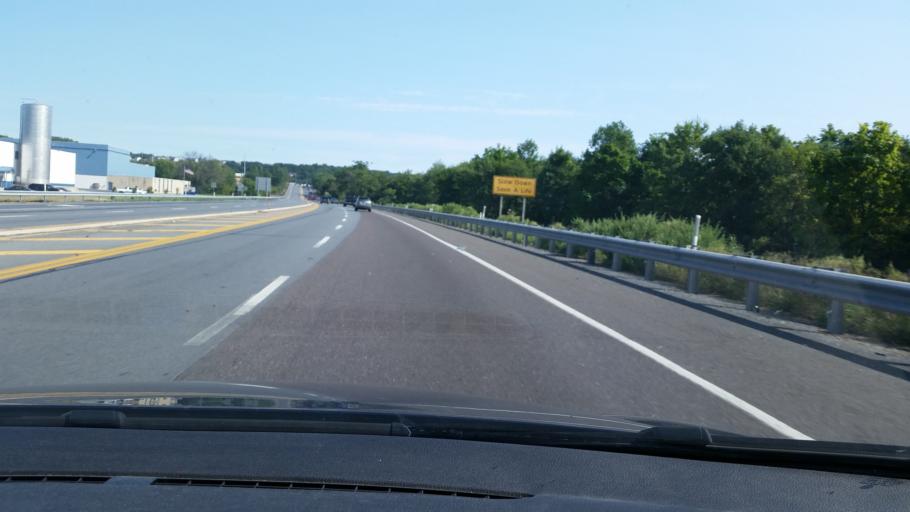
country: US
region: Pennsylvania
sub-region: Berks County
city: Hamburg
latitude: 40.5485
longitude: -75.9885
